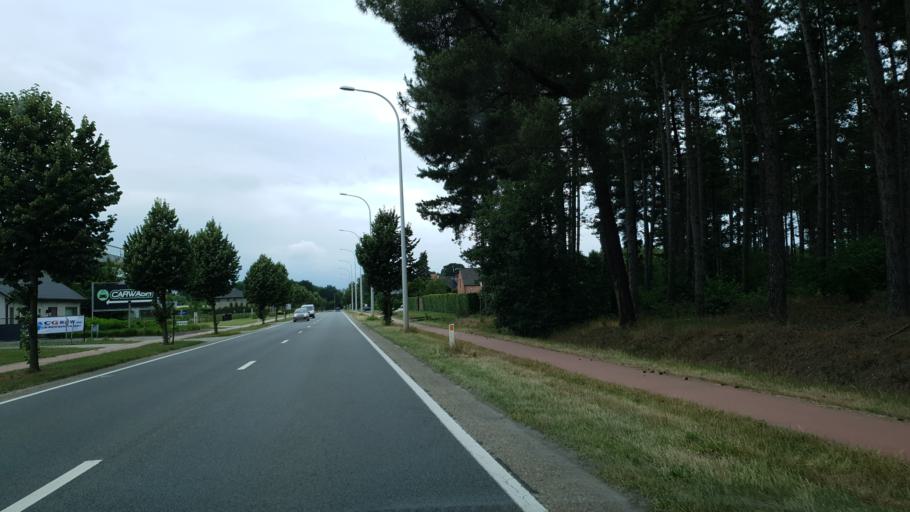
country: BE
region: Flanders
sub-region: Provincie Antwerpen
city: Laakdal
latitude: 51.1208
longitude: 5.0197
